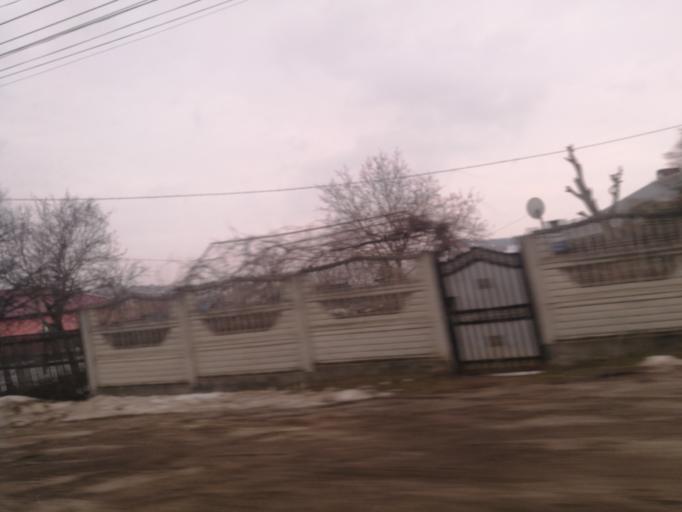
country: RO
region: Iasi
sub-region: Comuna Targu Frumos
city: Targu Frumos
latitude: 47.2042
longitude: 27.0006
